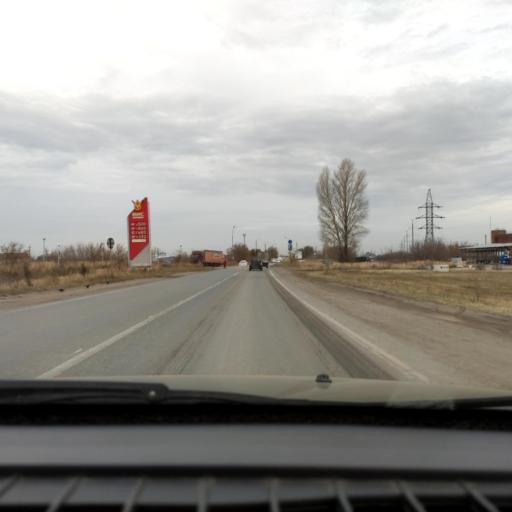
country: RU
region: Samara
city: Tol'yatti
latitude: 53.5716
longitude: 49.3421
